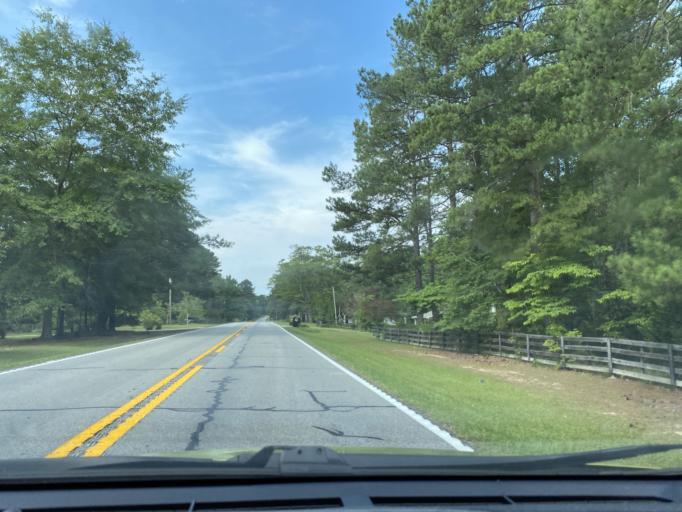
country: US
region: Georgia
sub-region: Coweta County
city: East Newnan
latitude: 33.2972
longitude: -84.6872
